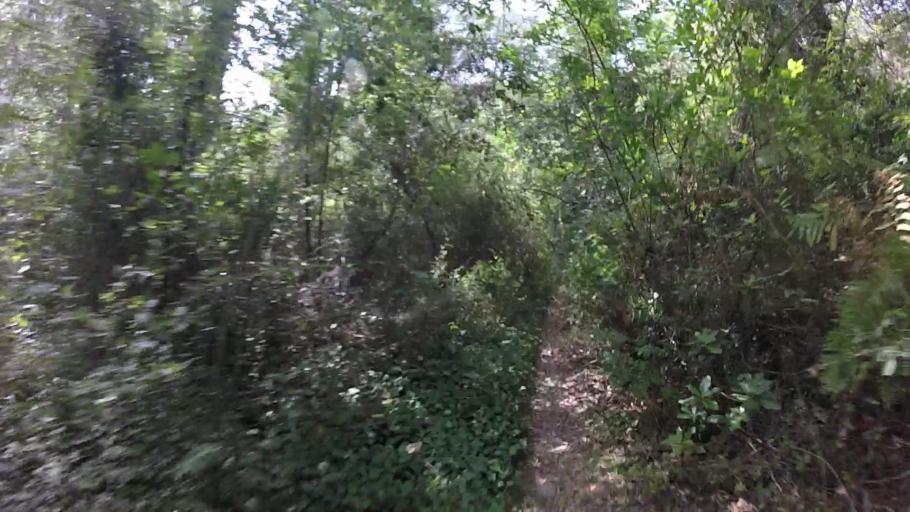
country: FR
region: Provence-Alpes-Cote d'Azur
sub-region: Departement des Alpes-Maritimes
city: Mougins
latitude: 43.6137
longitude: 7.0199
